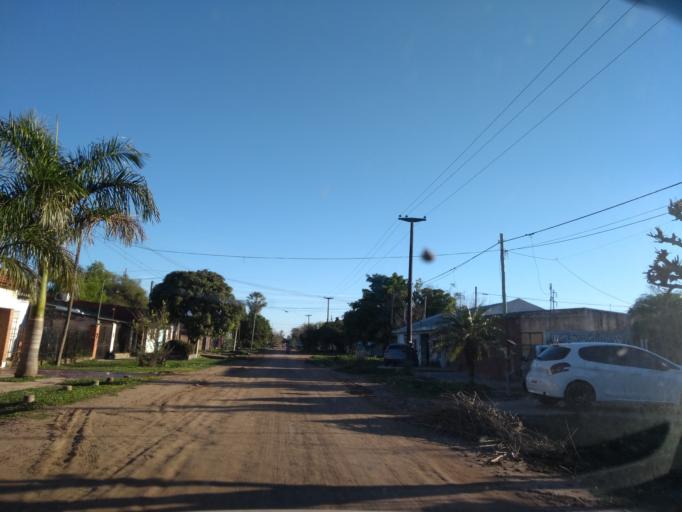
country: AR
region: Chaco
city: Barranqueras
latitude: -27.4896
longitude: -58.9348
